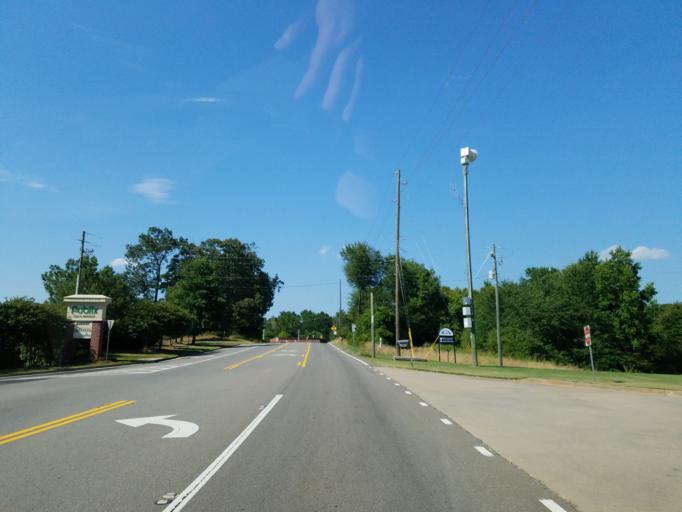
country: US
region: Georgia
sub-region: Fulton County
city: Milton
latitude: 34.2367
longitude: -84.2898
